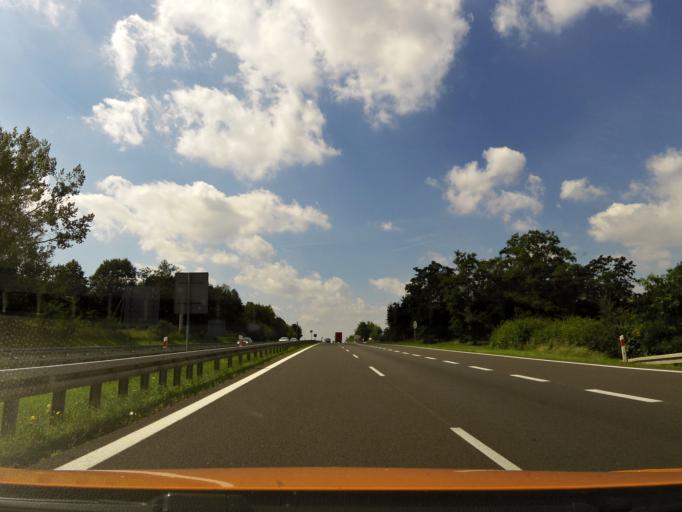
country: PL
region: West Pomeranian Voivodeship
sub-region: Powiat policki
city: Kolbaskowo
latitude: 53.3360
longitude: 14.4103
